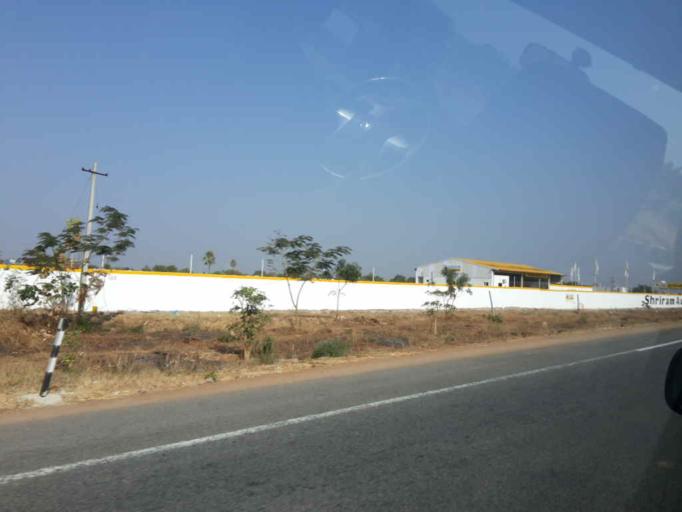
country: IN
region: Telangana
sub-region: Nizamabad District
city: Nizamabad
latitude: 18.7513
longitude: 78.2792
